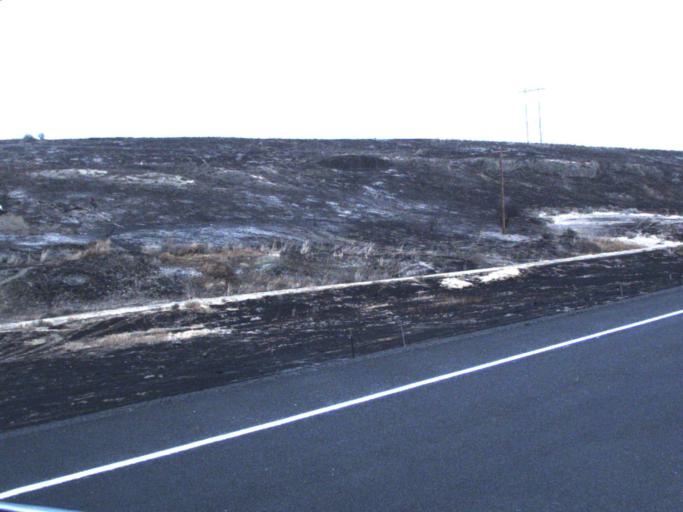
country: US
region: Washington
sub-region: Adams County
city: Ritzville
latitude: 47.3582
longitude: -118.5110
